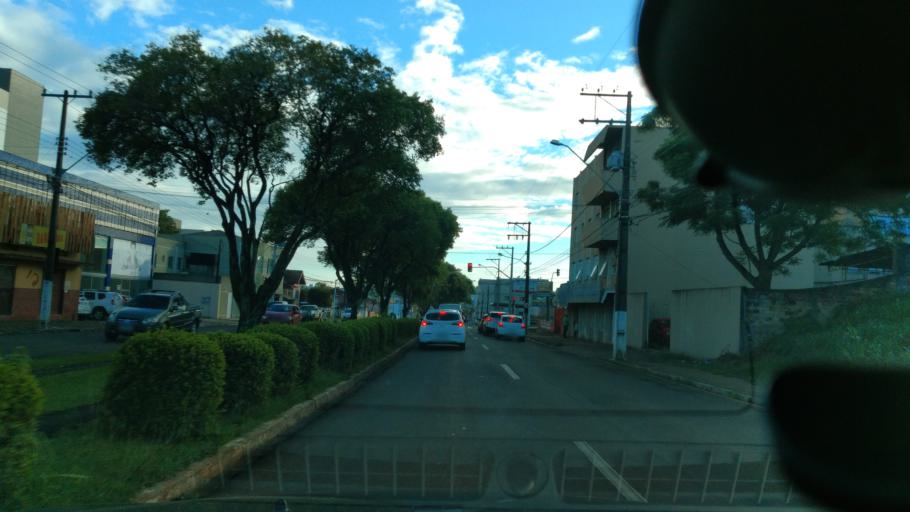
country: BR
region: Parana
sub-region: Guarapuava
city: Guarapuava
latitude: -25.3903
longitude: -51.4774
